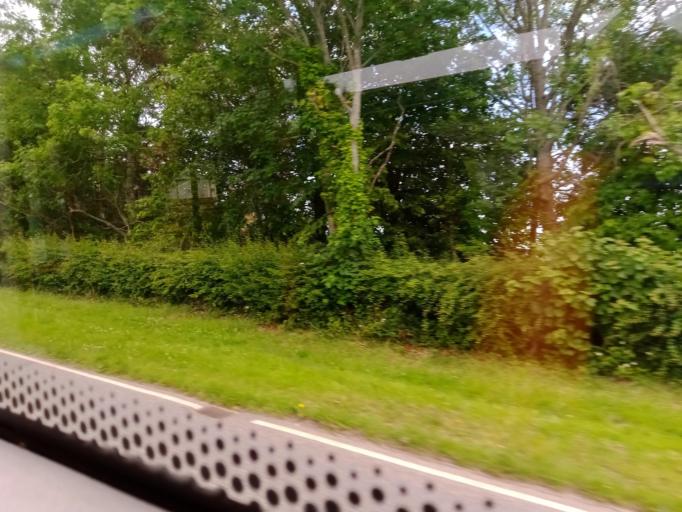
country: GB
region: Wales
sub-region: Anglesey
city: Llangoed
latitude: 53.2862
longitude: -4.0874
